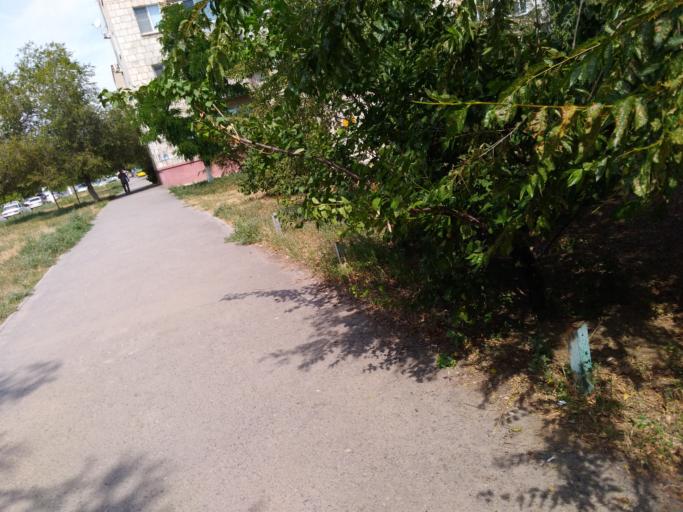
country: RU
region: Volgograd
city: Volgograd
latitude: 48.6992
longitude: 44.4922
